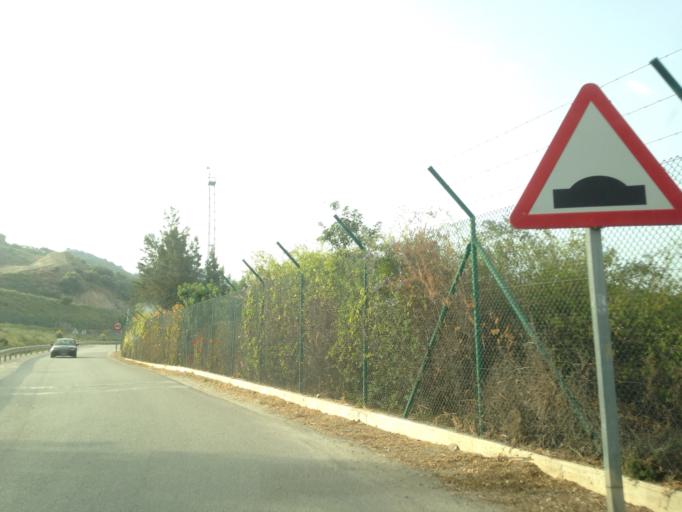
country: ES
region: Andalusia
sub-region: Provincia de Malaga
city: Estacion de Cartama
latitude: 36.7458
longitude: -4.5622
